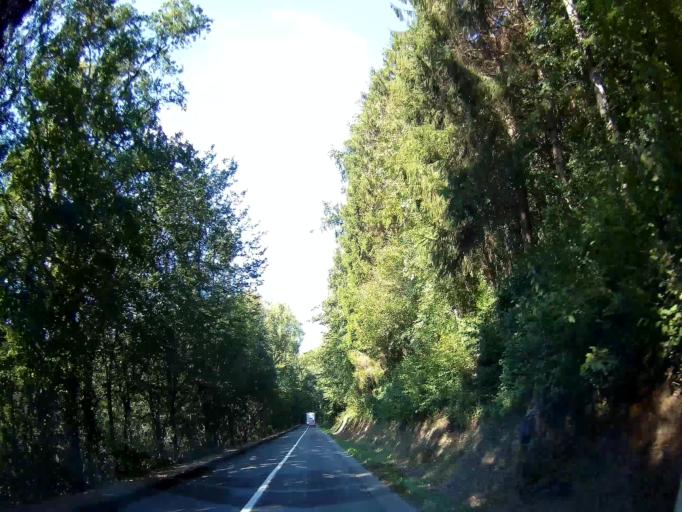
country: BE
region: Wallonia
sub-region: Province de Namur
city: Onhaye
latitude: 50.3037
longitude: 4.7626
